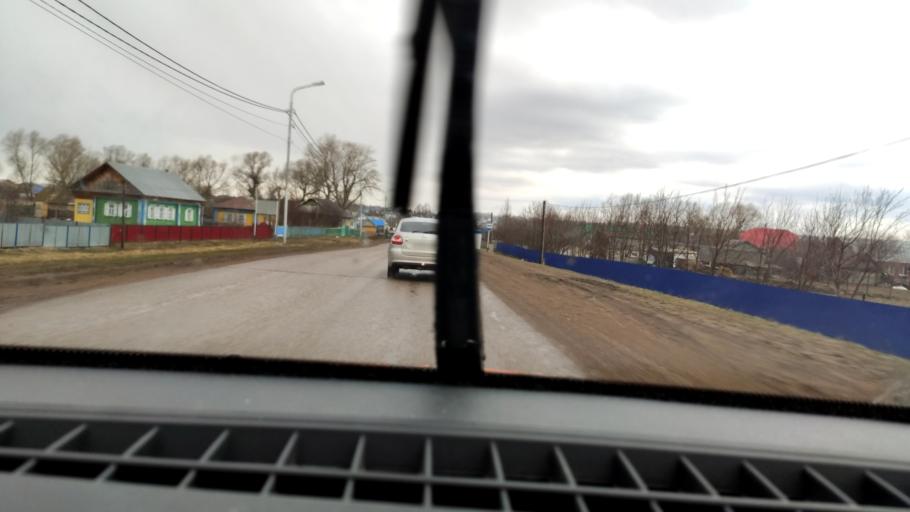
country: RU
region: Bashkortostan
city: Chekmagush
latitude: 55.1332
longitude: 54.6744
